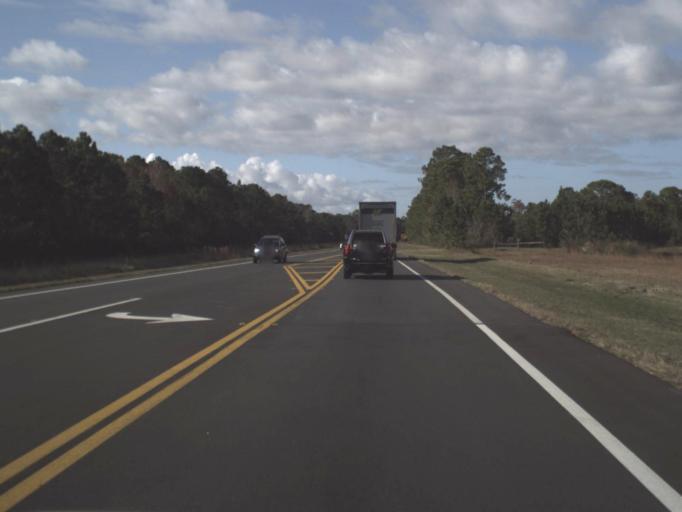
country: US
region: Florida
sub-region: Volusia County
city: South Daytona
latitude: 29.1364
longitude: -81.0525
